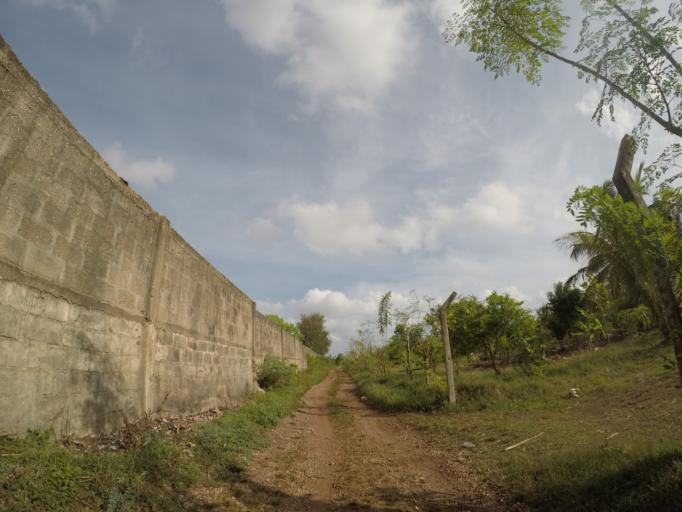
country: TZ
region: Zanzibar Central/South
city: Koani
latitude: -6.2248
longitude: 39.3087
